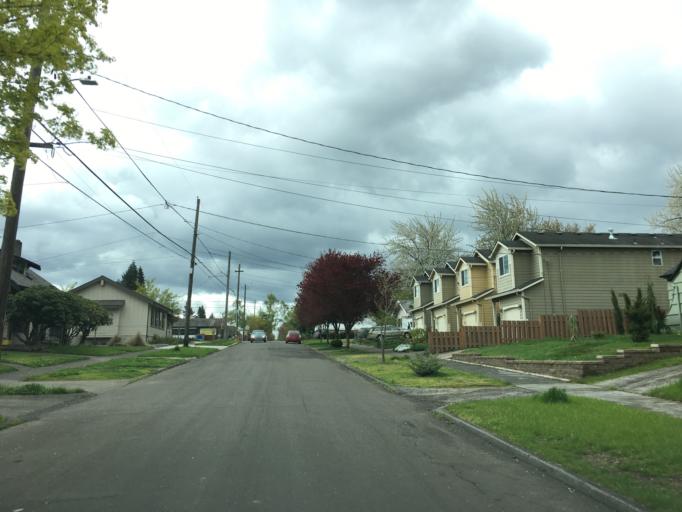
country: US
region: Oregon
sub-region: Multnomah County
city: Lents
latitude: 45.5508
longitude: -122.5848
